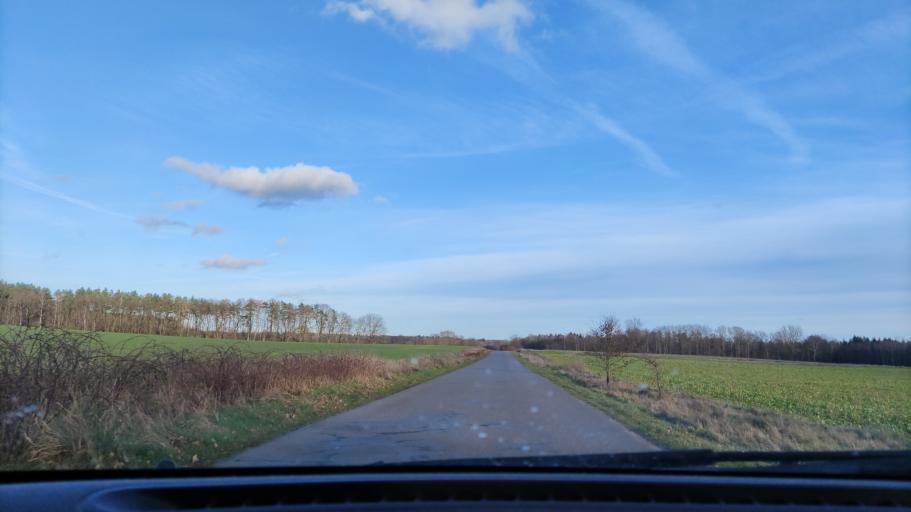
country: DE
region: Lower Saxony
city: Eimke
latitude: 52.9750
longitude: 10.3186
